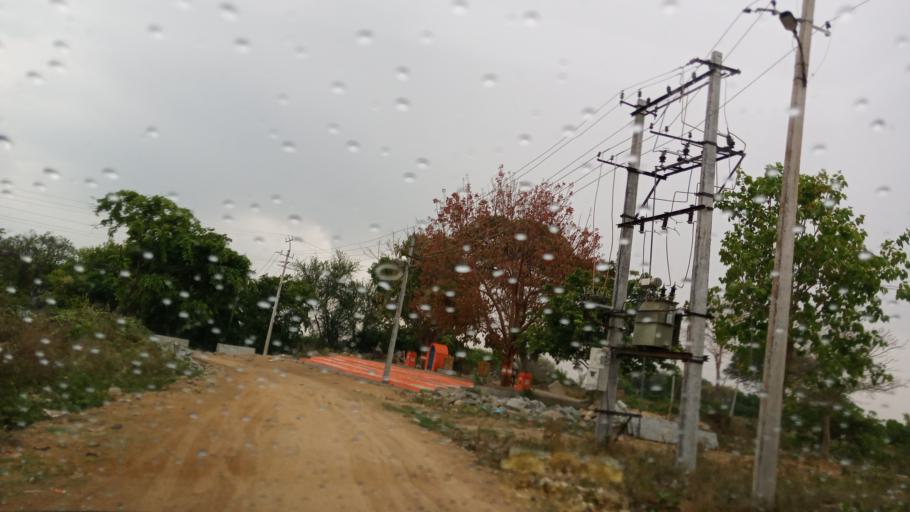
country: IN
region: Karnataka
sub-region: Kolar
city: Mulbagal
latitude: 13.1061
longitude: 78.3272
